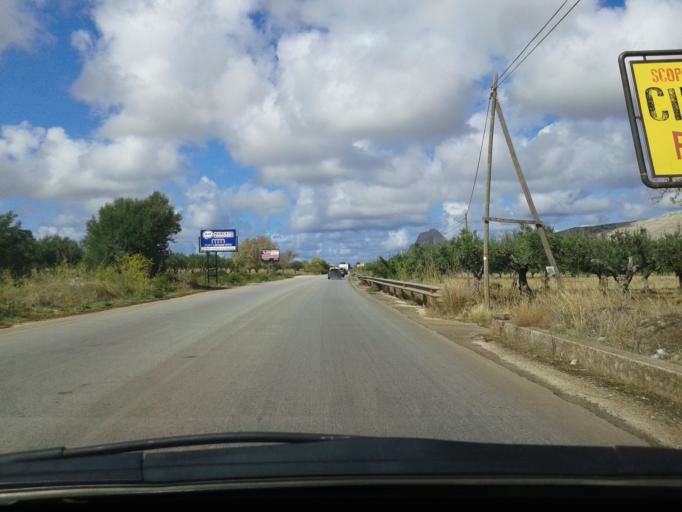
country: IT
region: Sicily
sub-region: Trapani
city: Castelluzzo
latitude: 38.0765
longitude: 12.7304
